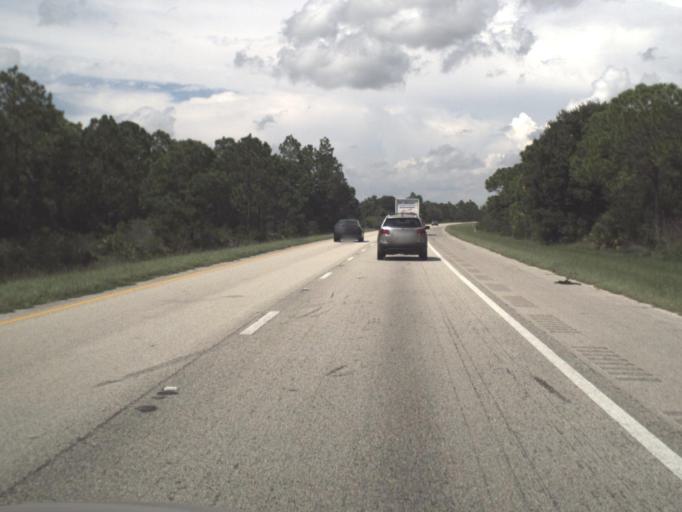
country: US
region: Florida
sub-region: Lee County
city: Suncoast Estates
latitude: 26.7804
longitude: -81.8946
